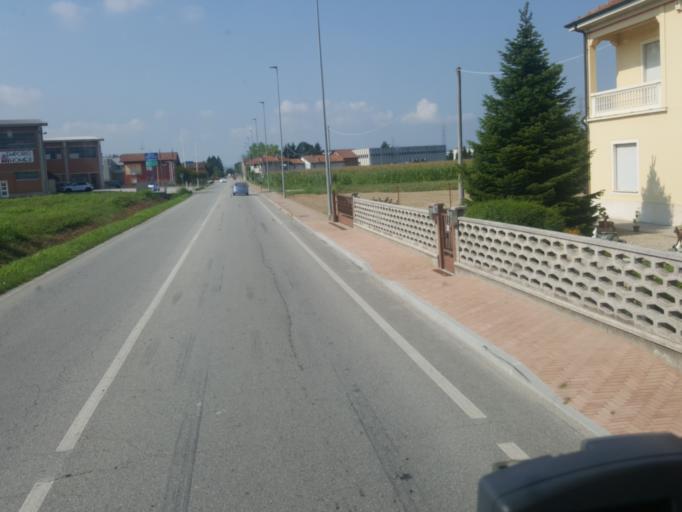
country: IT
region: Piedmont
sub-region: Provincia di Cuneo
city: Vaccheria
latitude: 44.7268
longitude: 8.0428
